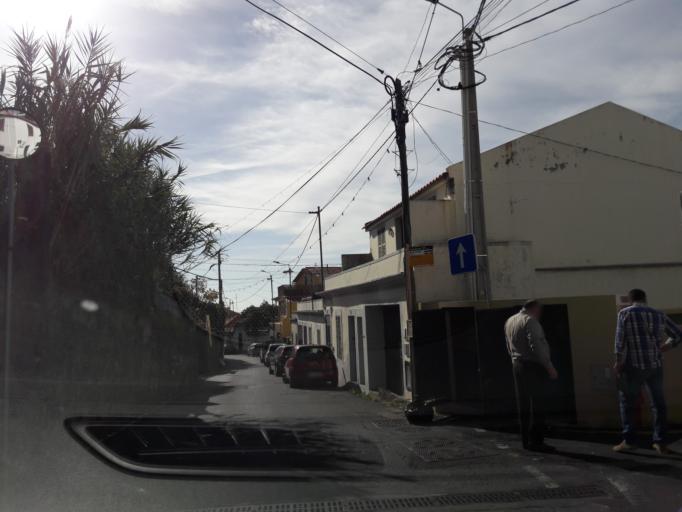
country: PT
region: Madeira
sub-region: Funchal
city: Nossa Senhora do Monte
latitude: 32.6650
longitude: -16.9229
